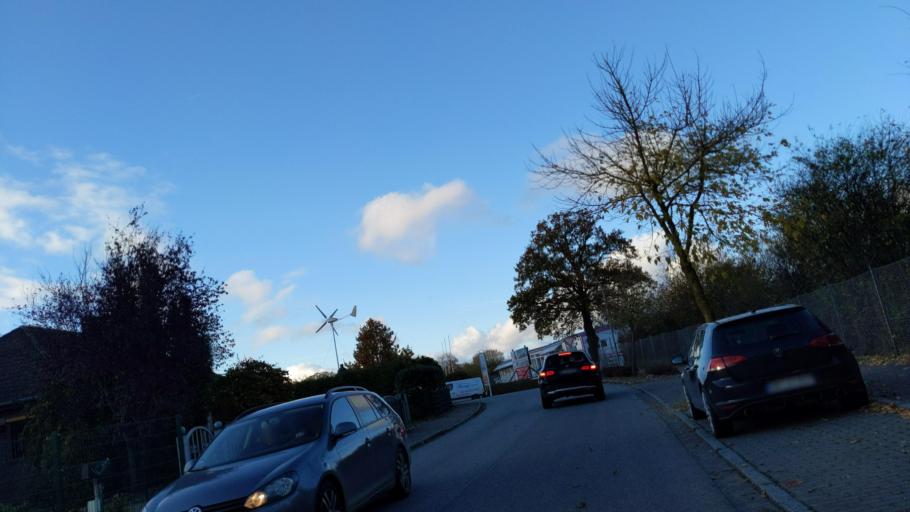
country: DE
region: Schleswig-Holstein
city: Neustadt in Holstein
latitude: 54.0944
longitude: 10.7897
